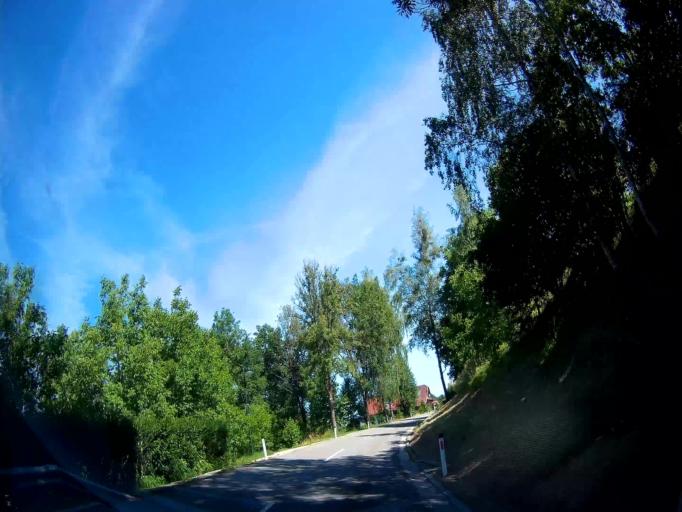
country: AT
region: Carinthia
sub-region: Politischer Bezirk Sankt Veit an der Glan
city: St. Georgen am Laengsee
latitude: 46.7665
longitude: 14.4208
